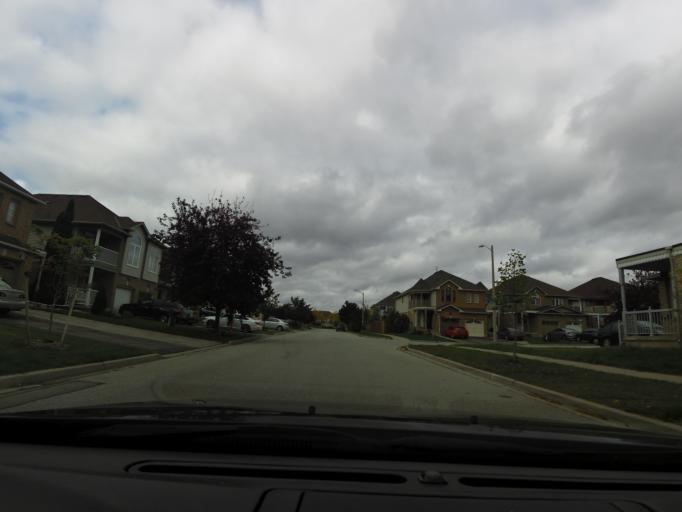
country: CA
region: Ontario
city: Burlington
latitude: 43.3920
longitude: -79.7833
